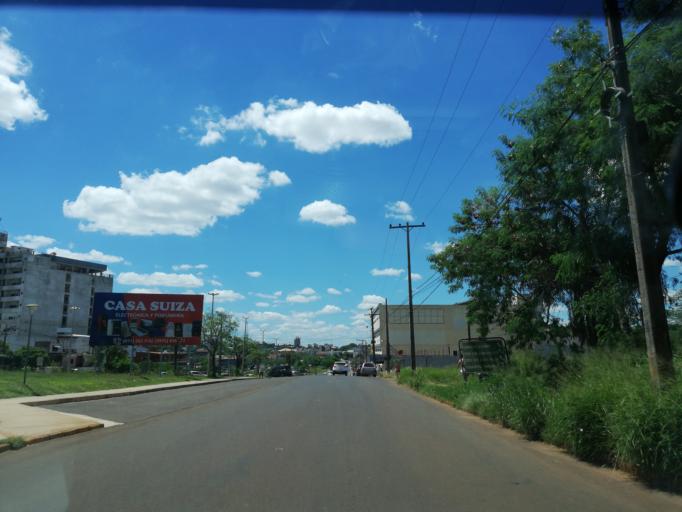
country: PY
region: Itapua
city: Encarnacion
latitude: -27.3530
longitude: -55.8582
